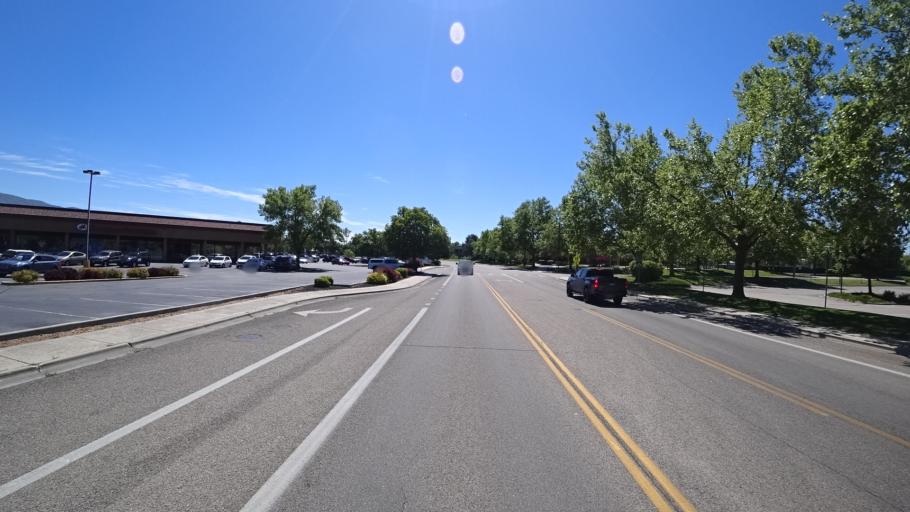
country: US
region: Idaho
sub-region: Ada County
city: Boise
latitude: 43.5798
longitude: -116.1762
